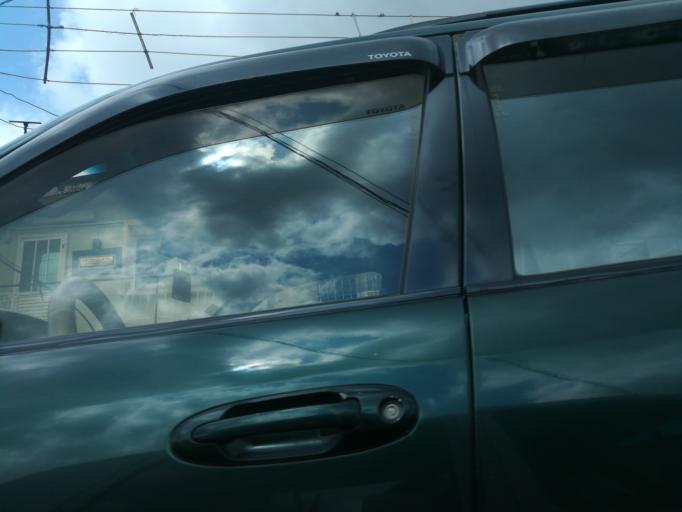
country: NG
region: Lagos
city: Somolu
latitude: 6.5399
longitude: 3.3618
